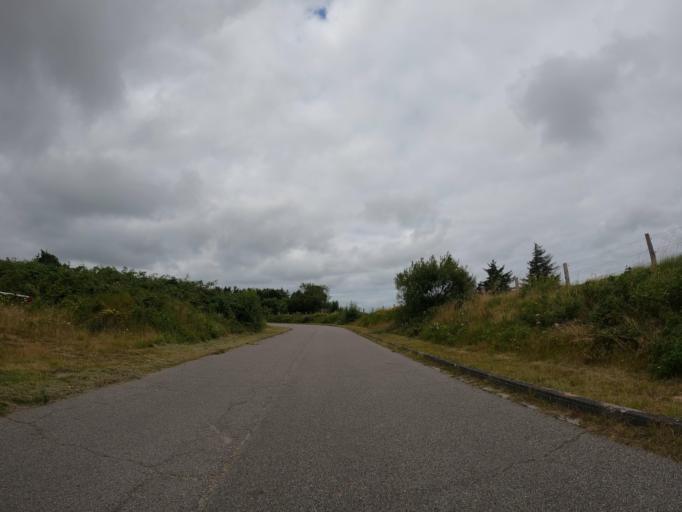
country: DE
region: Schleswig-Holstein
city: Tinnum
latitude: 54.9217
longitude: 8.3453
